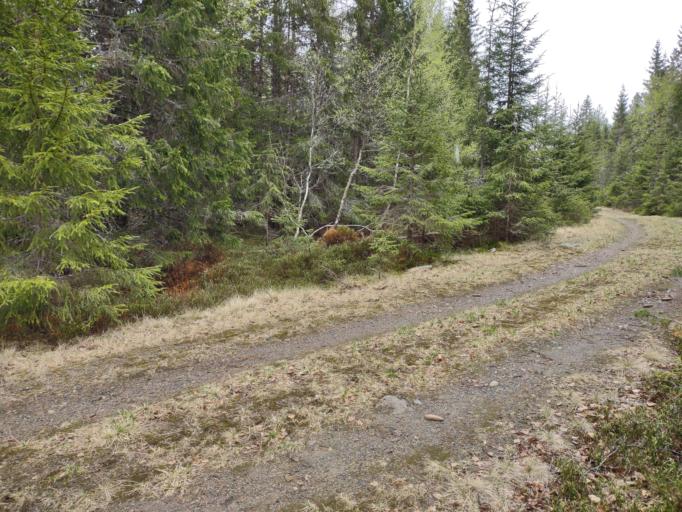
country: NO
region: Oppland
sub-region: Lunner
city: Grua
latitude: 60.3346
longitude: 10.8004
